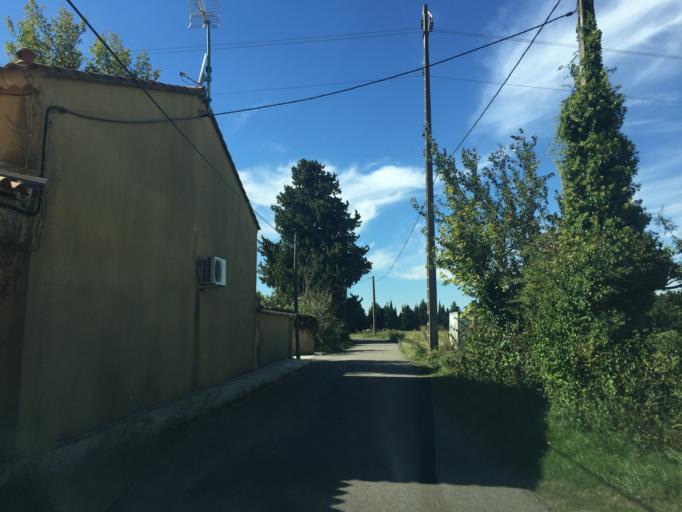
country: FR
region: Provence-Alpes-Cote d'Azur
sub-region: Departement du Vaucluse
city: Orange
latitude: 44.1545
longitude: 4.7910
